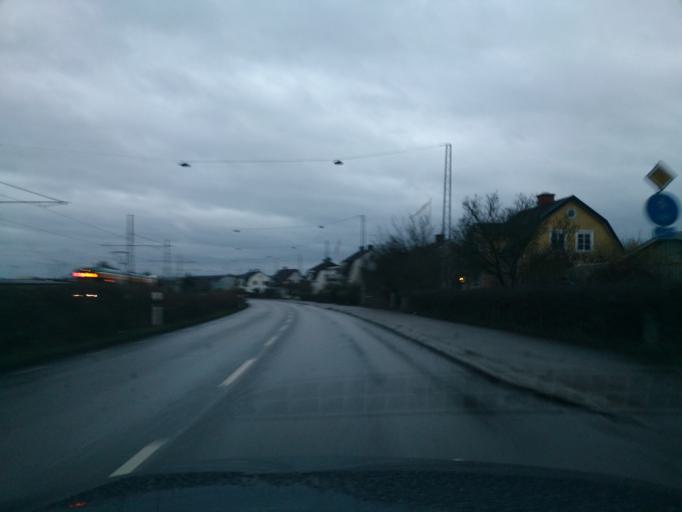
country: SE
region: OEstergoetland
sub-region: Norrkopings Kommun
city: Norrkoping
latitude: 58.6050
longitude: 16.1394
